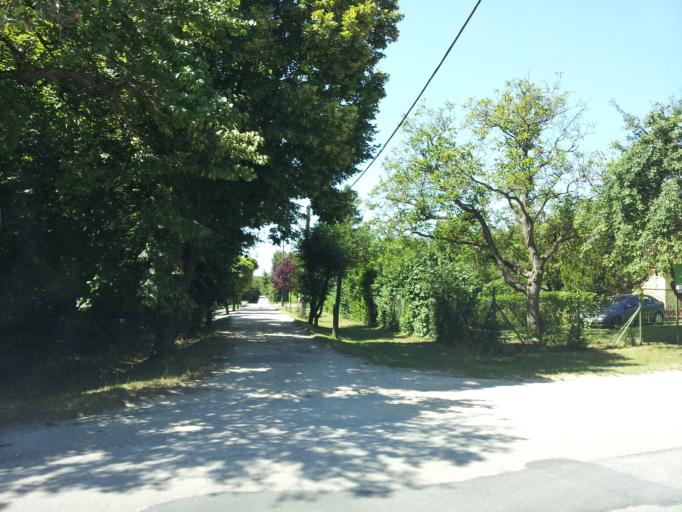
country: HU
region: Veszprem
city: Balatonkenese
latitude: 47.0199
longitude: 18.1597
